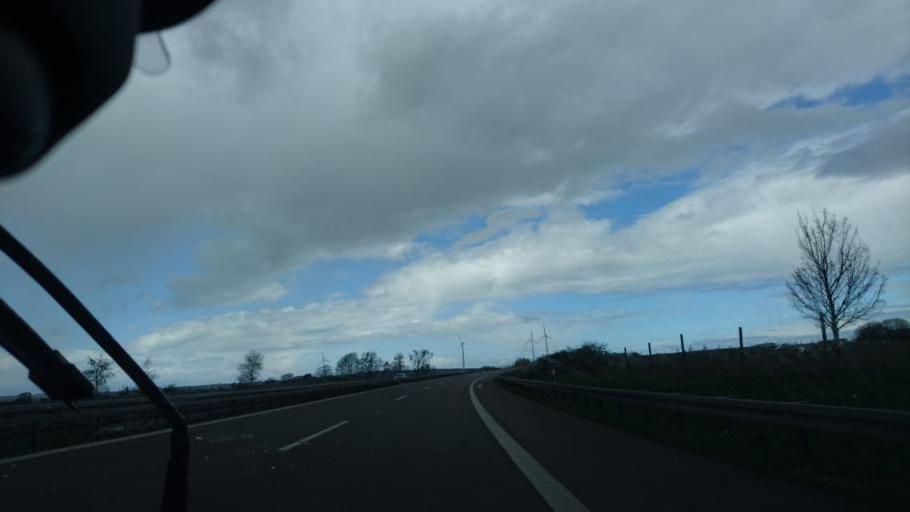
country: DE
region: Mecklenburg-Vorpommern
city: Kritzmow
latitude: 54.0400
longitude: 12.0416
